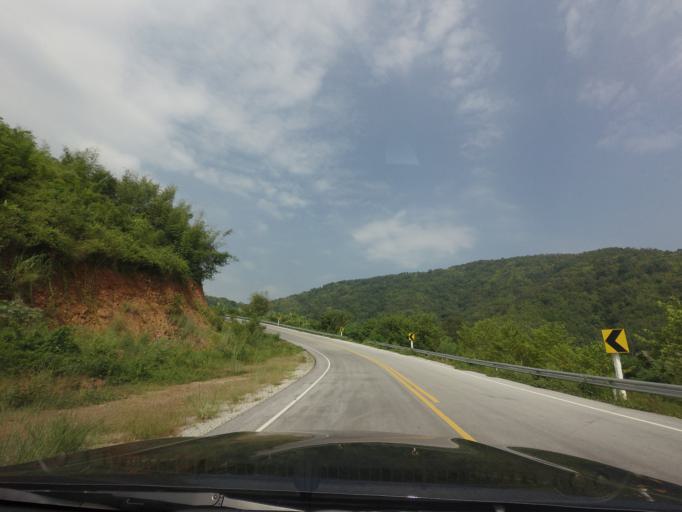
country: LA
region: Xiagnabouli
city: Muang Kenthao
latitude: 17.7750
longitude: 101.5233
